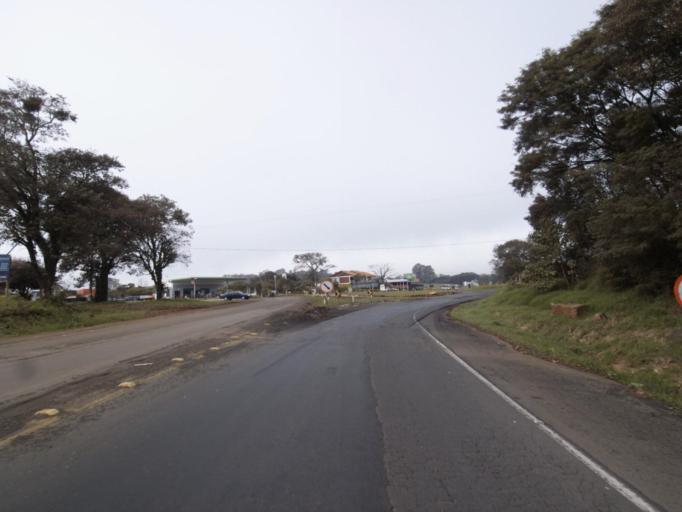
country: BR
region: Rio Grande do Sul
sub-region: Frederico Westphalen
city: Frederico Westphalen
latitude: -27.1020
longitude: -53.2121
